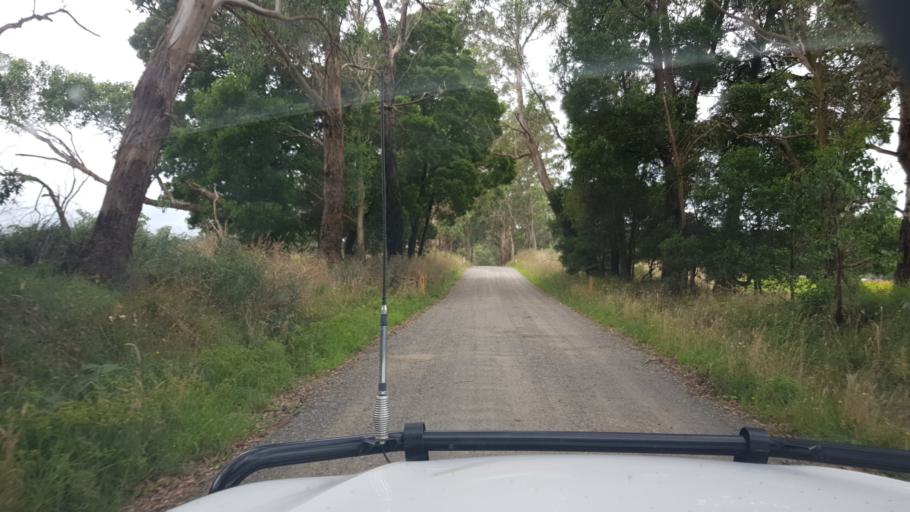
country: AU
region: Victoria
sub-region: Baw Baw
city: Warragul
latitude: -38.2216
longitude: 145.8402
